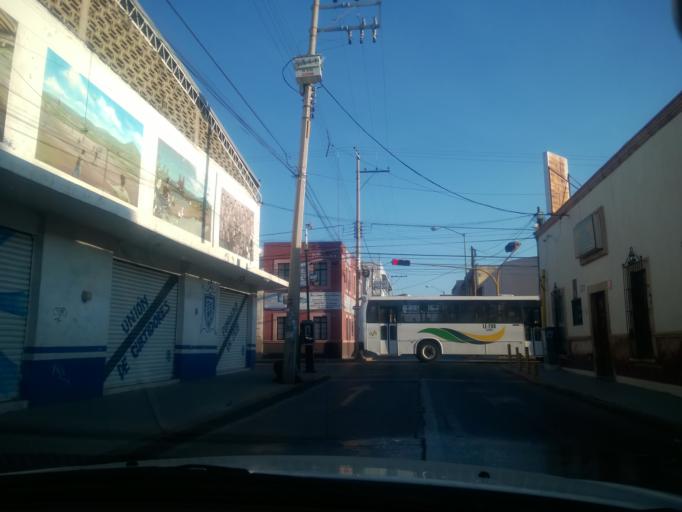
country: MX
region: Guanajuato
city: Leon
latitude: 21.1271
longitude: -101.6833
